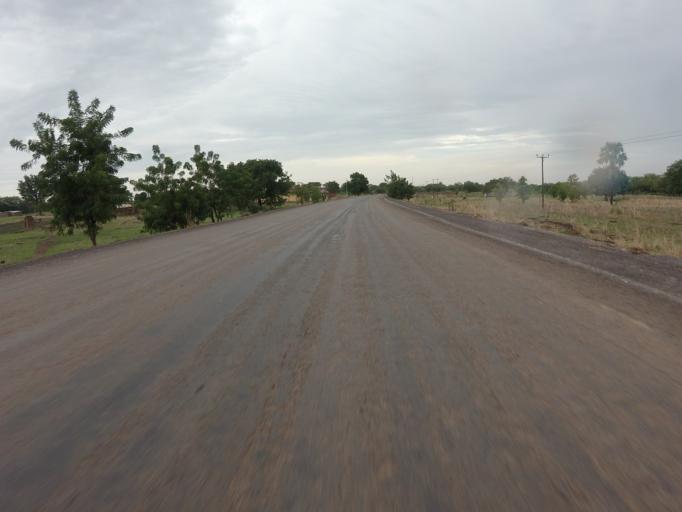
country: GH
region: Upper East
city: Bolgatanga
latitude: 10.8645
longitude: -0.6590
